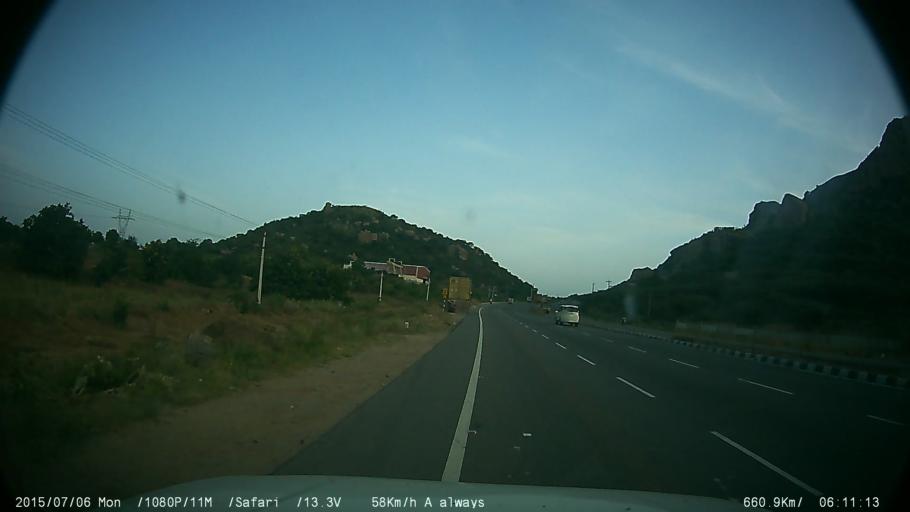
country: IN
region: Tamil Nadu
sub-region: Krishnagiri
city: Kelamangalam
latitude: 12.6549
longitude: 78.0243
